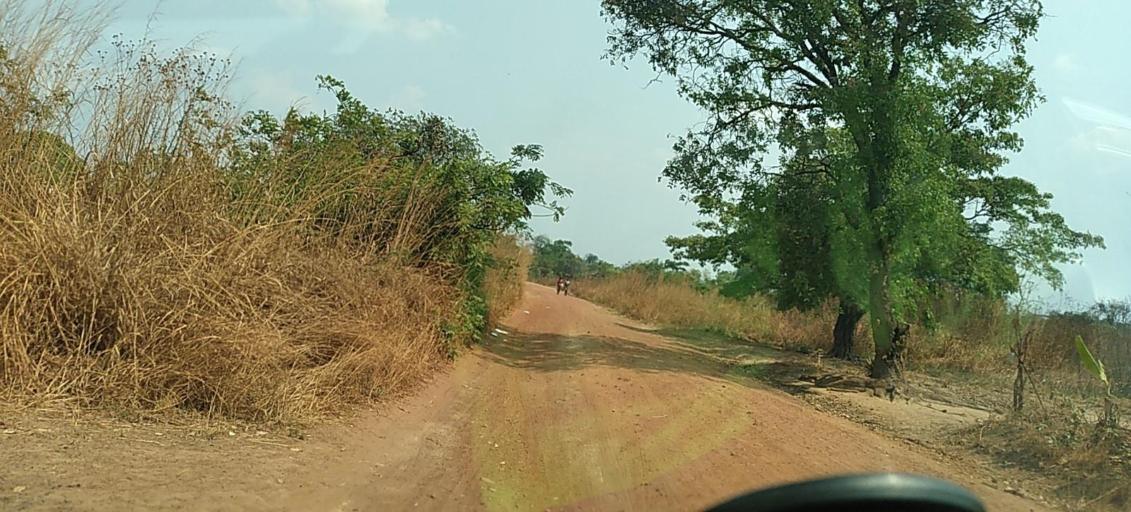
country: ZM
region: North-Western
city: Kansanshi
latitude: -12.0978
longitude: 26.3632
